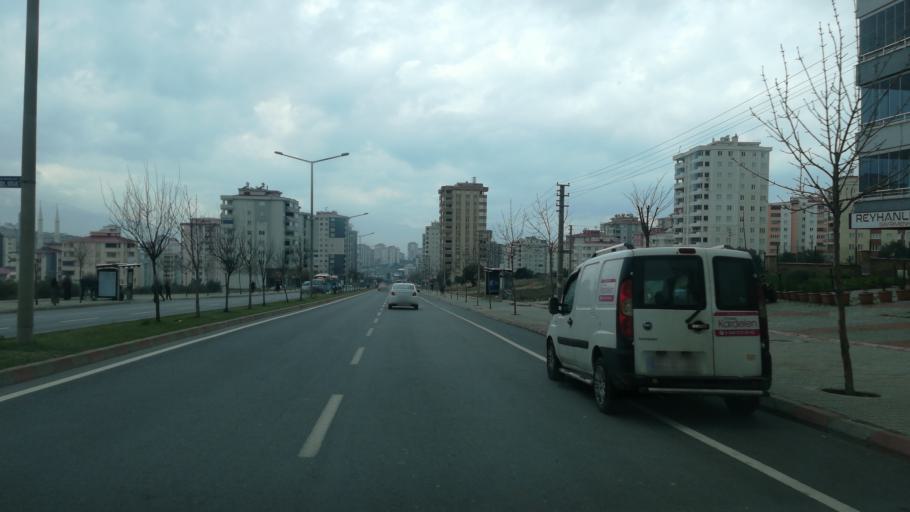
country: TR
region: Kahramanmaras
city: Kahramanmaras
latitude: 37.5832
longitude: 36.8782
